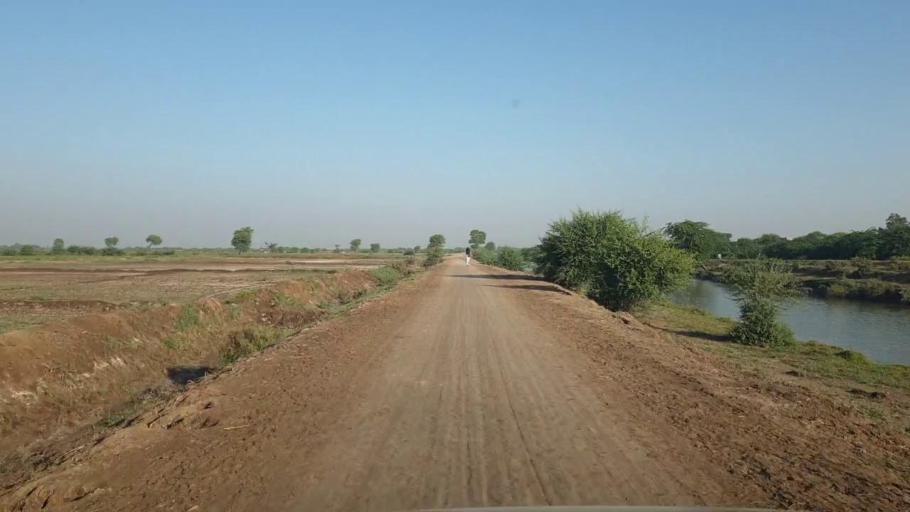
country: PK
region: Sindh
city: Badin
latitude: 24.6806
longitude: 68.8165
